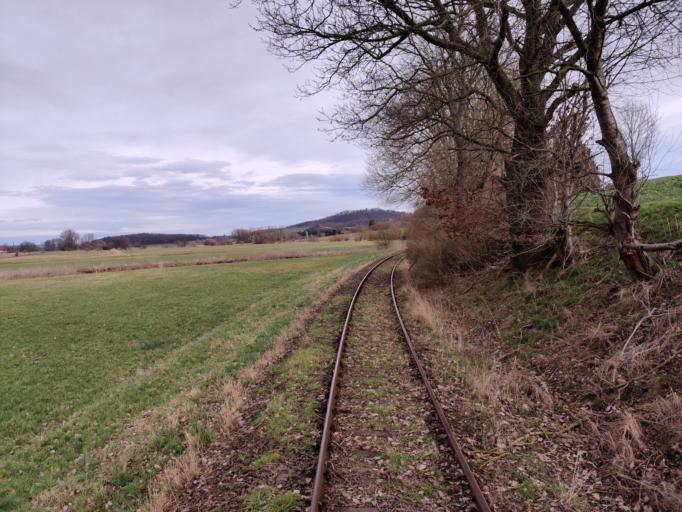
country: DE
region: Lower Saxony
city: Bockenem
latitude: 52.0450
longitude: 10.1231
